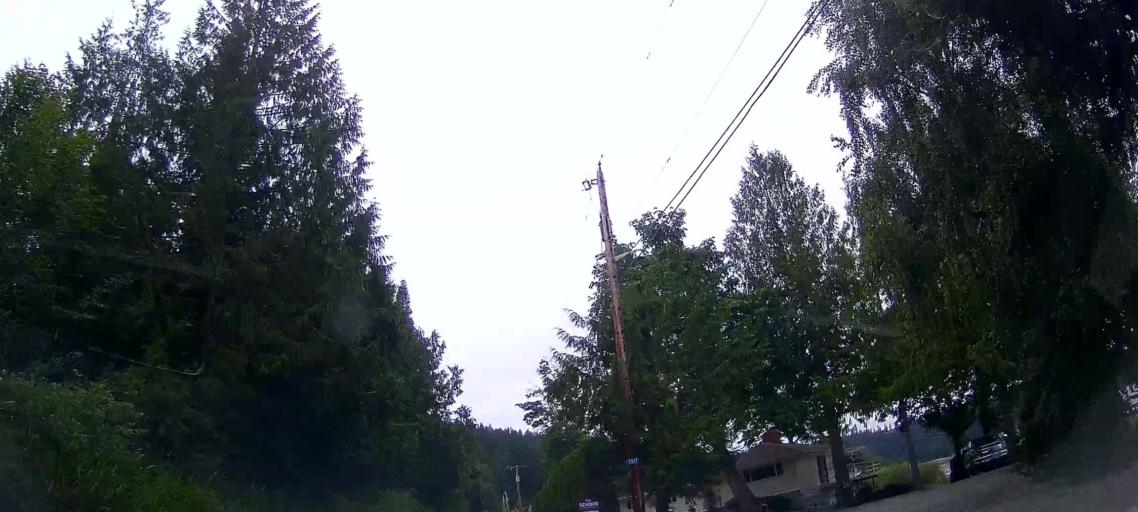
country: US
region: Washington
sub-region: Skagit County
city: Anacortes
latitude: 48.4336
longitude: -122.6181
